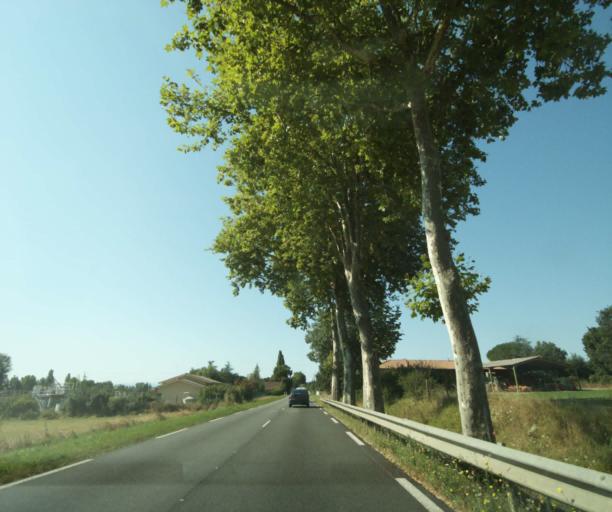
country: FR
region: Midi-Pyrenees
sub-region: Departement de la Haute-Garonne
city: Saint-Sulpice-sur-Leze
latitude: 43.3427
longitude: 1.3229
